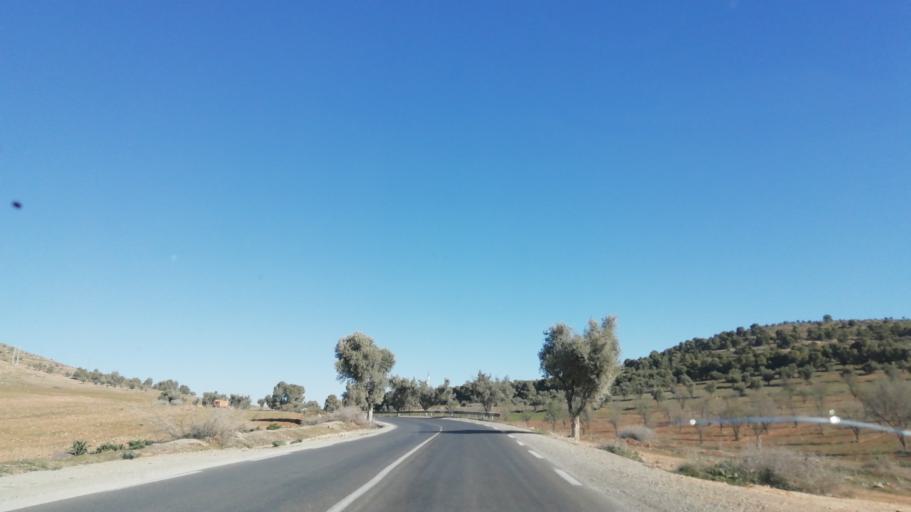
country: DZ
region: Mascara
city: Mascara
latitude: 35.2414
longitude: 0.1185
